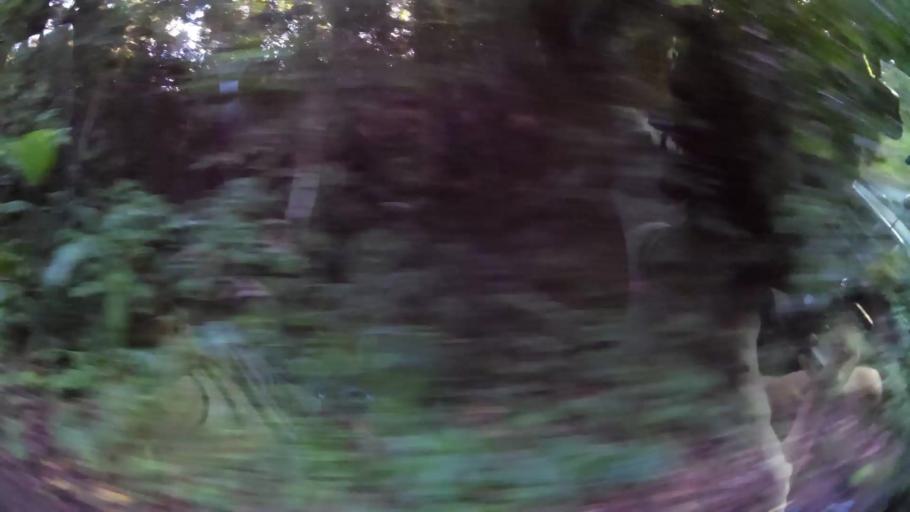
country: DM
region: Saint Andrew
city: Calibishie
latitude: 15.5915
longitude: -61.3607
